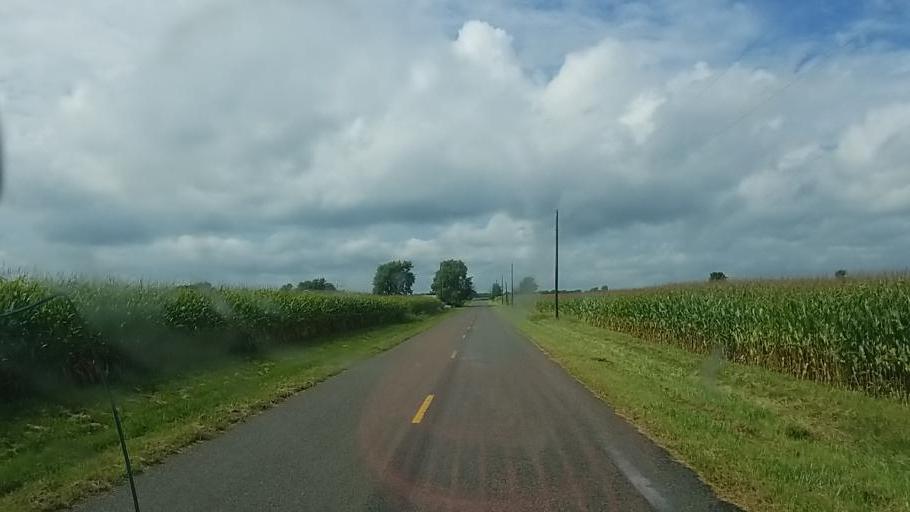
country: US
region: Ohio
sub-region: Hardin County
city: Kenton
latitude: 40.4869
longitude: -83.5154
